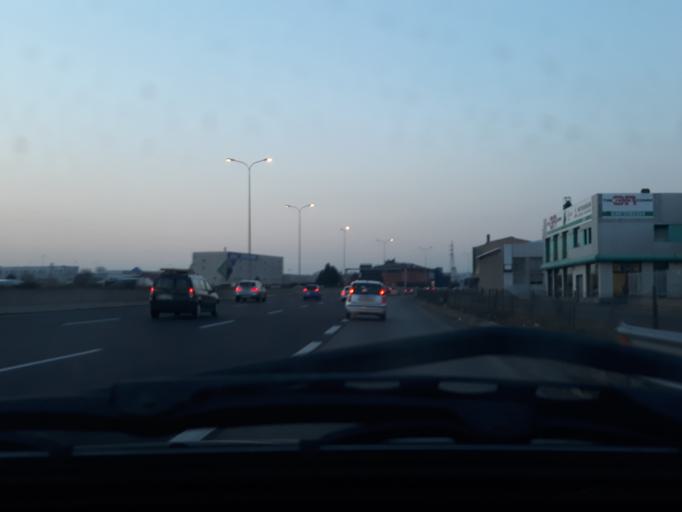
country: IT
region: Lombardy
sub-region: Provincia di Monza e Brianza
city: Lissone
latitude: 45.6073
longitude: 9.2256
